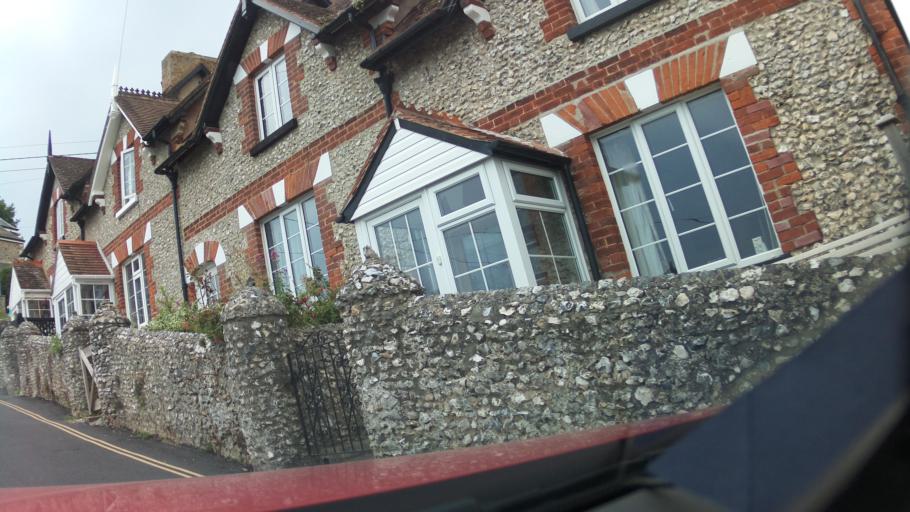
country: GB
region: England
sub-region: Devon
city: Colyton
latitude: 50.6965
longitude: -3.0924
